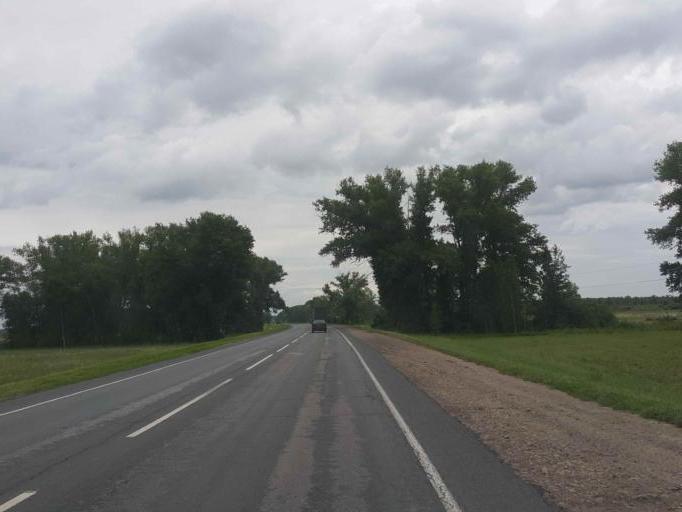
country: RU
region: Tambov
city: Zavoronezhskoye
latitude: 52.9519
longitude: 40.5821
